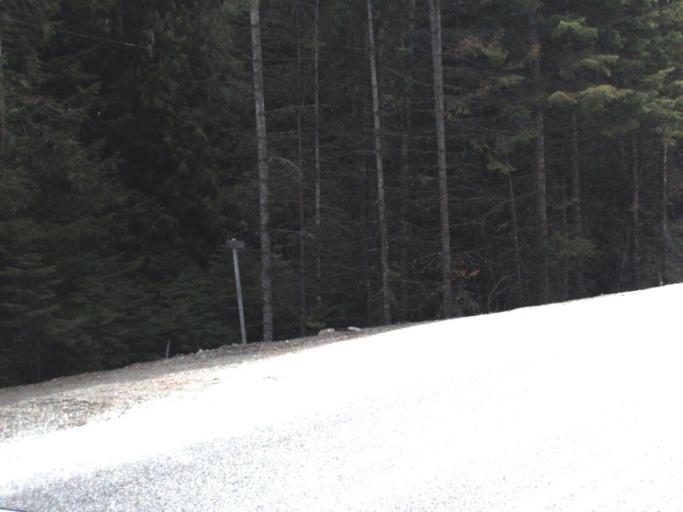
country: US
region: Washington
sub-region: Pend Oreille County
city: Newport
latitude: 48.5156
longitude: -117.2837
